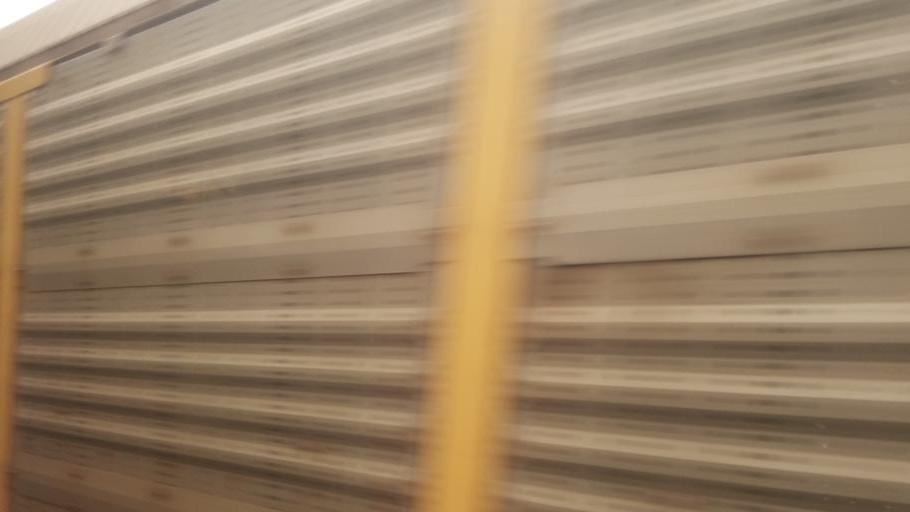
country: US
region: Pennsylvania
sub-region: Somerset County
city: Milford
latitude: 39.8797
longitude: -79.1055
